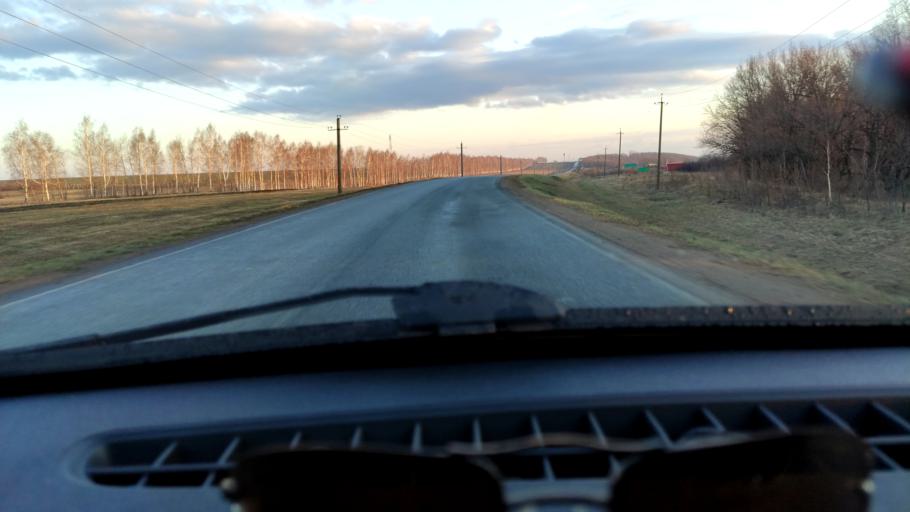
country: RU
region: Bashkortostan
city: Kabakovo
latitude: 54.5112
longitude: 56.1623
